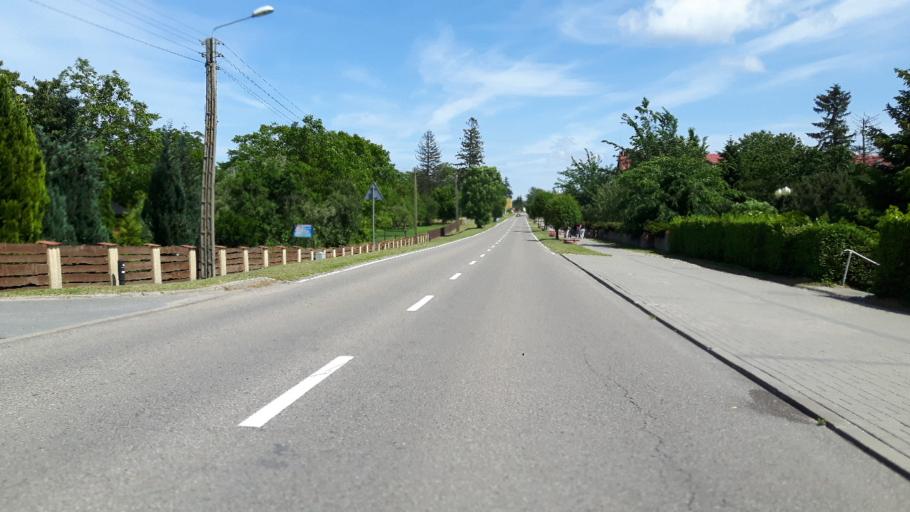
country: PL
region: Pomeranian Voivodeship
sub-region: Powiat wejherowski
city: Gniewino
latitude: 54.7167
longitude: 18.0195
